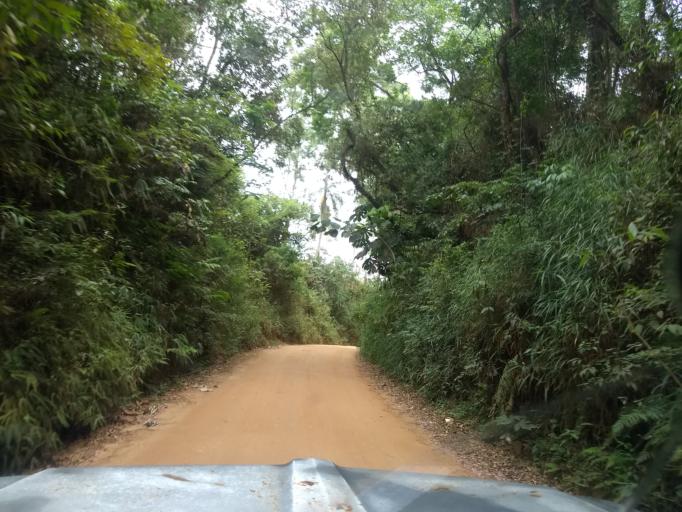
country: BR
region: Sao Paulo
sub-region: Cabreuva
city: Cabreuva
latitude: -23.4110
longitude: -47.2001
